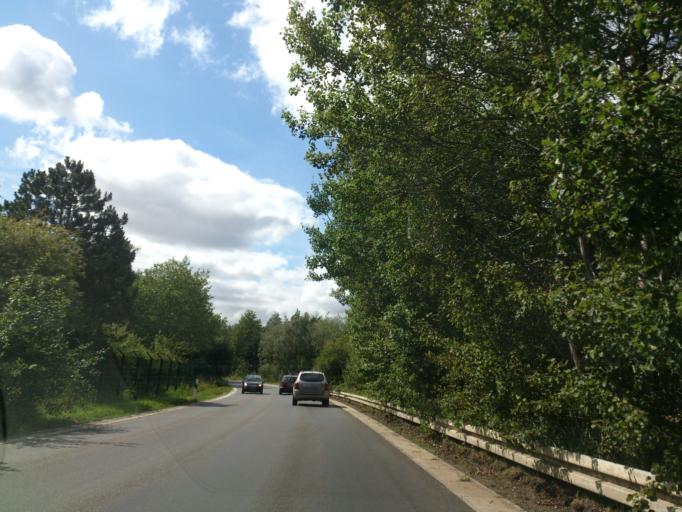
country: DE
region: Schleswig-Holstein
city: Flensburg
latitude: 54.8175
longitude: 9.4204
